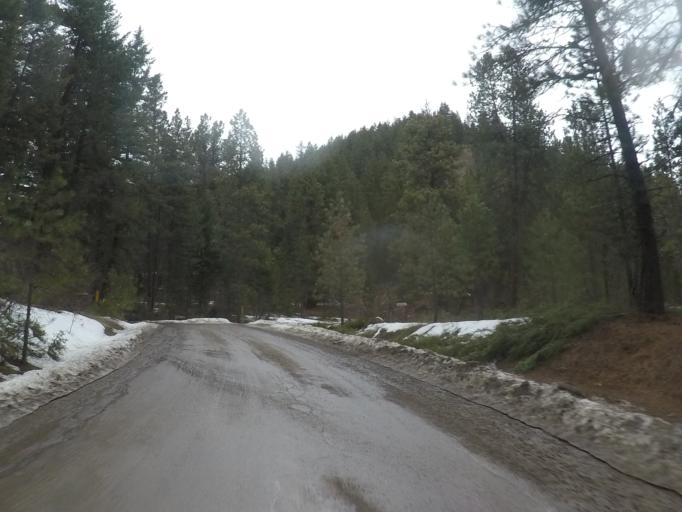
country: US
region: Montana
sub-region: Missoula County
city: East Missoula
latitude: 46.9240
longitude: -113.9614
